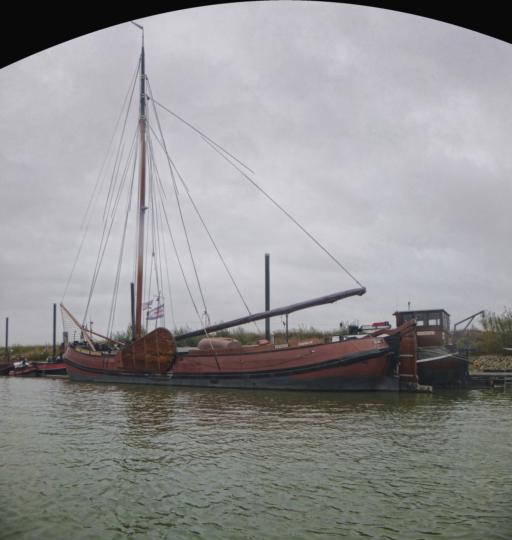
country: NL
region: Gelderland
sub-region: Gemeente Zutphen
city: Zutphen
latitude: 52.1494
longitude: 6.1875
